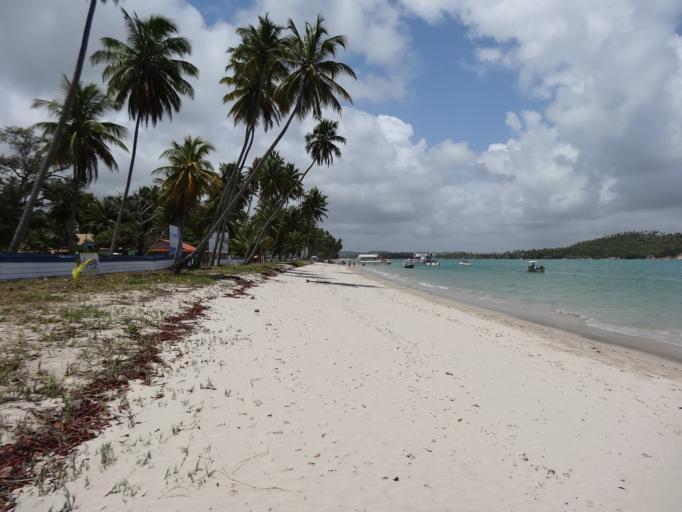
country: BR
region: Pernambuco
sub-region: Tamandare
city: Tamandare
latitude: -8.6964
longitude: -35.0891
